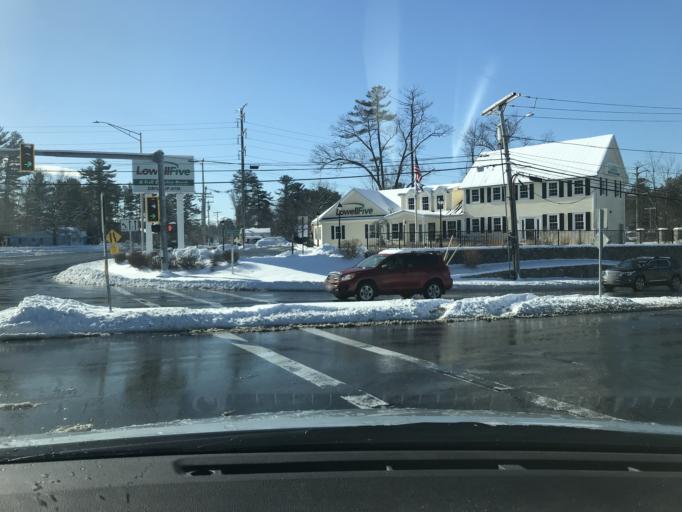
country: US
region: New Hampshire
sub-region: Hillsborough County
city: Nashua
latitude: 42.7317
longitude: -71.4710
